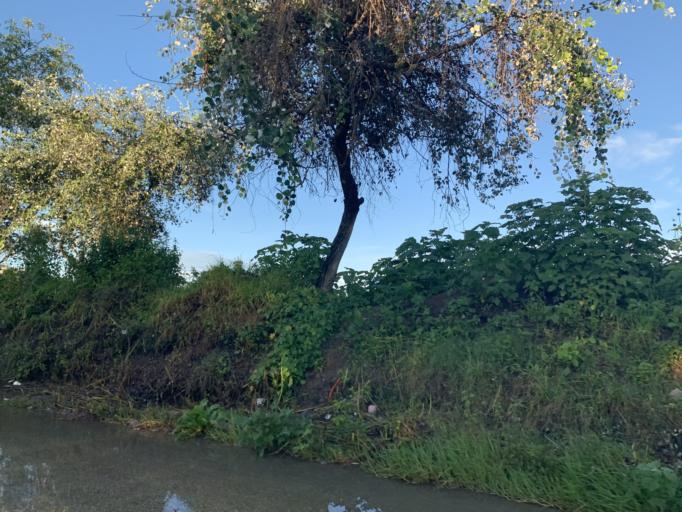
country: MX
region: Puebla
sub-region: Cuautlancingo
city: Sanctorum
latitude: 19.0926
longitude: -98.2496
